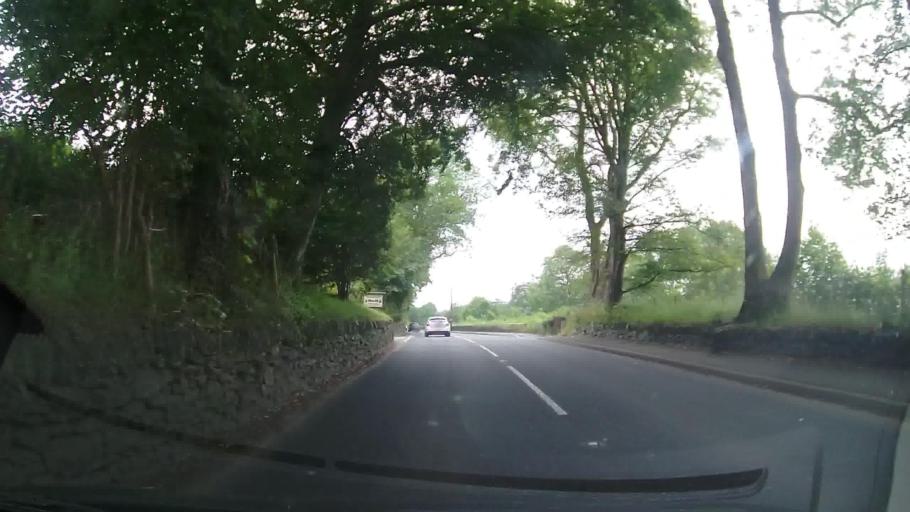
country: GB
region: Wales
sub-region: Denbighshire
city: Corwen
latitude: 52.9810
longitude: -3.3581
